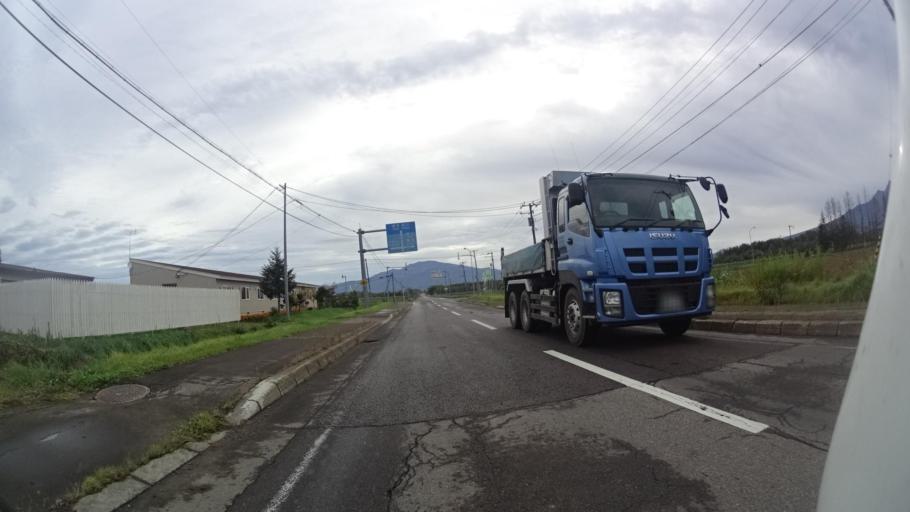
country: JP
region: Hokkaido
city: Abashiri
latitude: 43.8706
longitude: 144.6616
